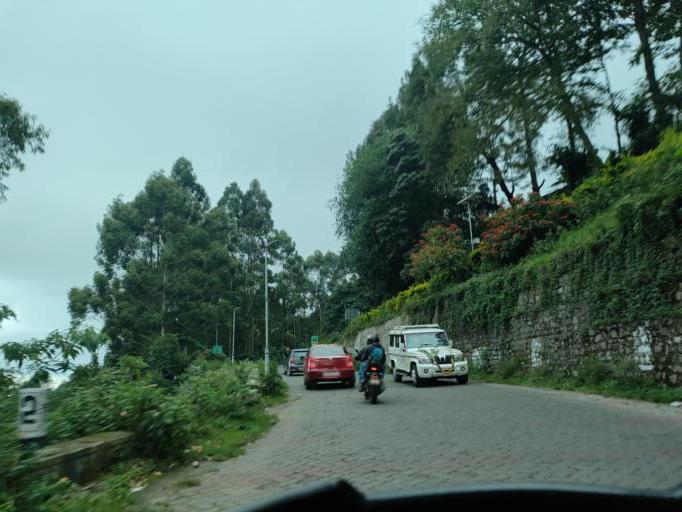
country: IN
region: Tamil Nadu
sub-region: Dindigul
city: Kodaikanal
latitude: 10.2307
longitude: 77.5022
